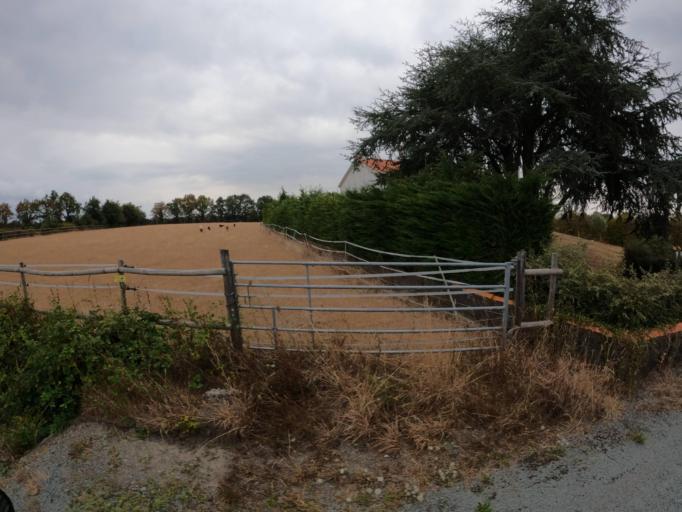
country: FR
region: Pays de la Loire
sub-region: Departement de la Vendee
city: Treize-Septiers
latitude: 46.9800
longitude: -1.2146
